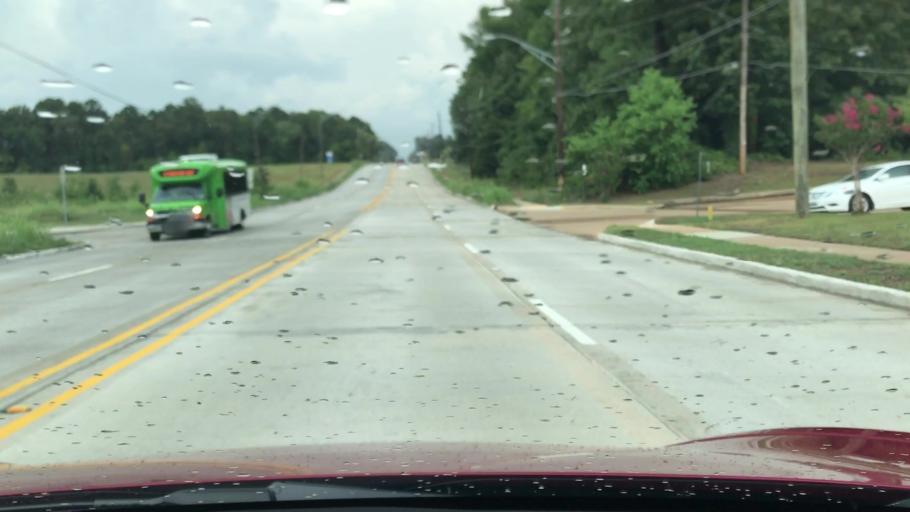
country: US
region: Louisiana
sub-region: Bossier Parish
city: Bossier City
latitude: 32.3998
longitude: -93.7633
